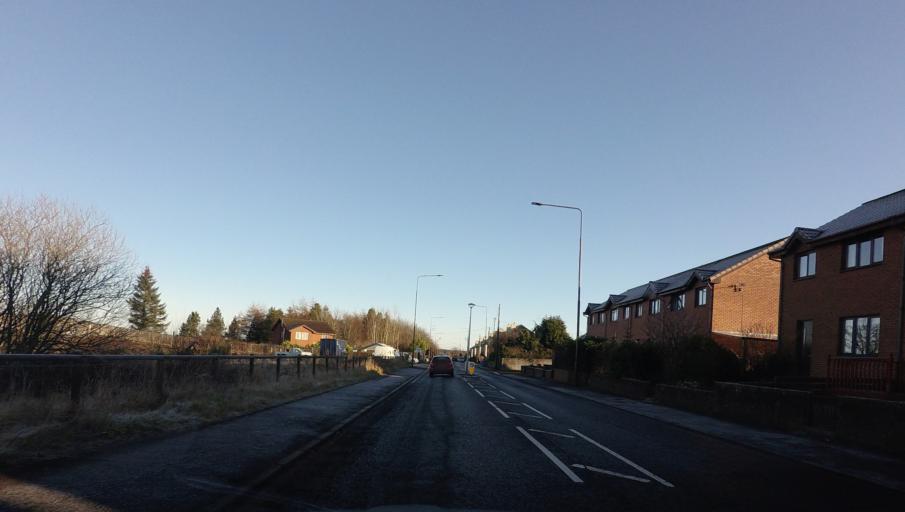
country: GB
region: Scotland
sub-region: West Lothian
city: Blackburn
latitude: 55.8294
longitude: -3.6581
